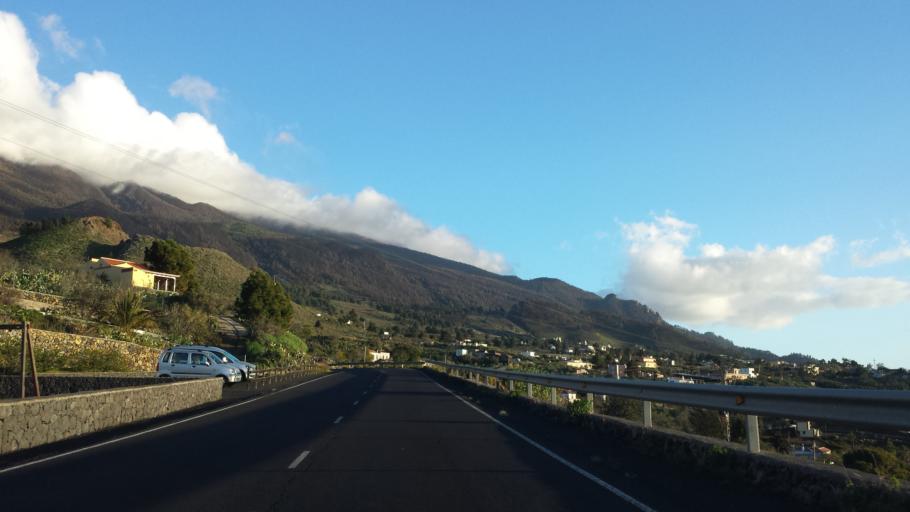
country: ES
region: Canary Islands
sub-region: Provincia de Santa Cruz de Tenerife
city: El Paso
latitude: 28.6169
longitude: -17.8851
